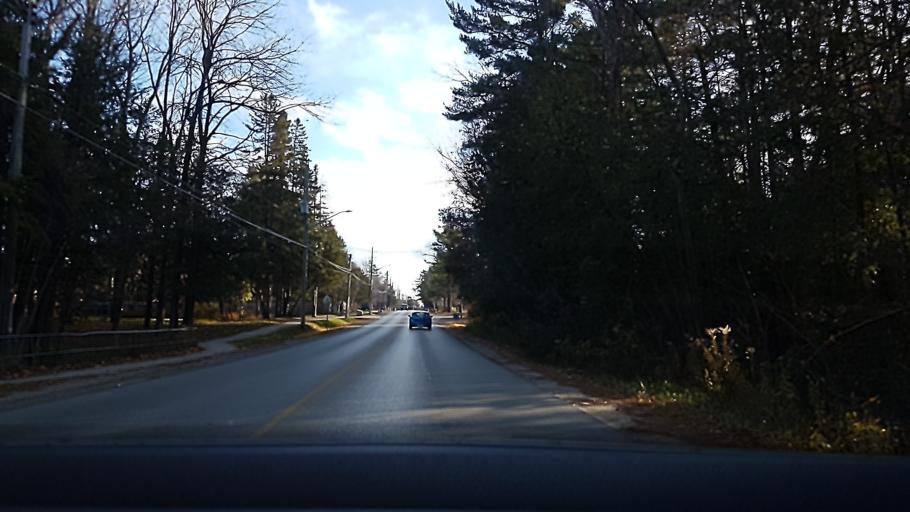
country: CA
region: Ontario
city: Keswick
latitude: 44.3273
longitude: -79.5425
